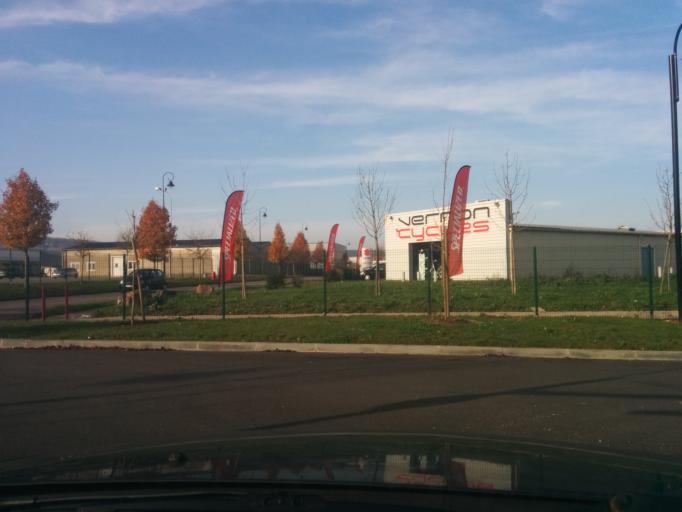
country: FR
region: Haute-Normandie
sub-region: Departement de l'Eure
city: Saint-Marcel
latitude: 49.1004
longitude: 1.4580
